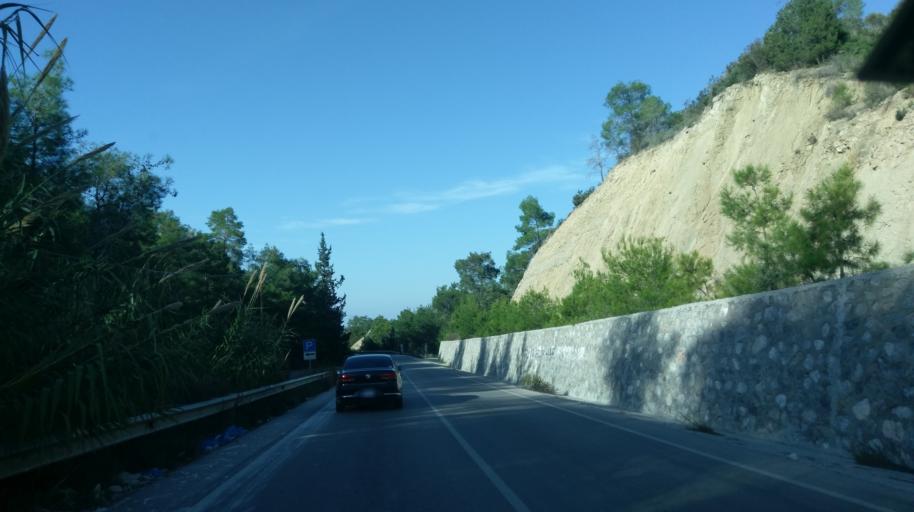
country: CY
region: Ammochostos
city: Lefkonoiko
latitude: 35.3560
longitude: 33.7124
